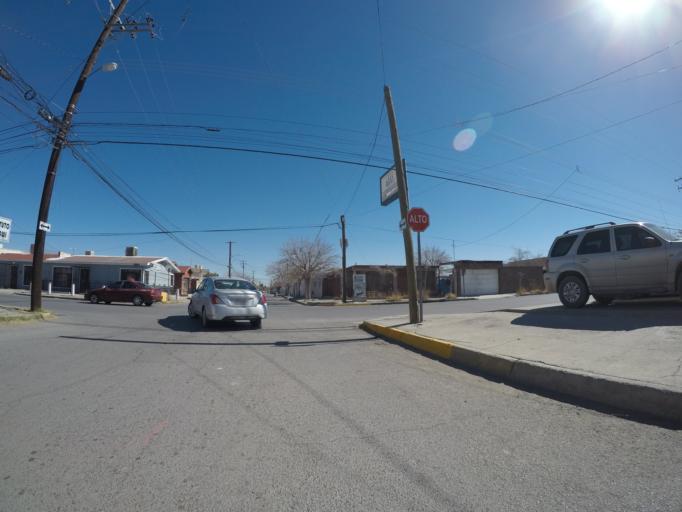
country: MX
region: Chihuahua
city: Ciudad Juarez
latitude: 31.7324
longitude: -106.4455
